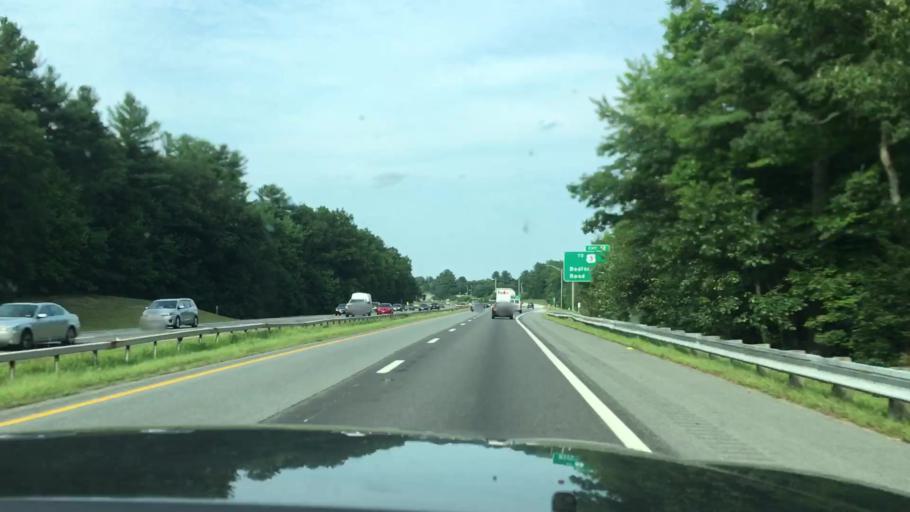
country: US
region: New Hampshire
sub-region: Hillsborough County
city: East Merrimack
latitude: 42.8796
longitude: -71.4855
